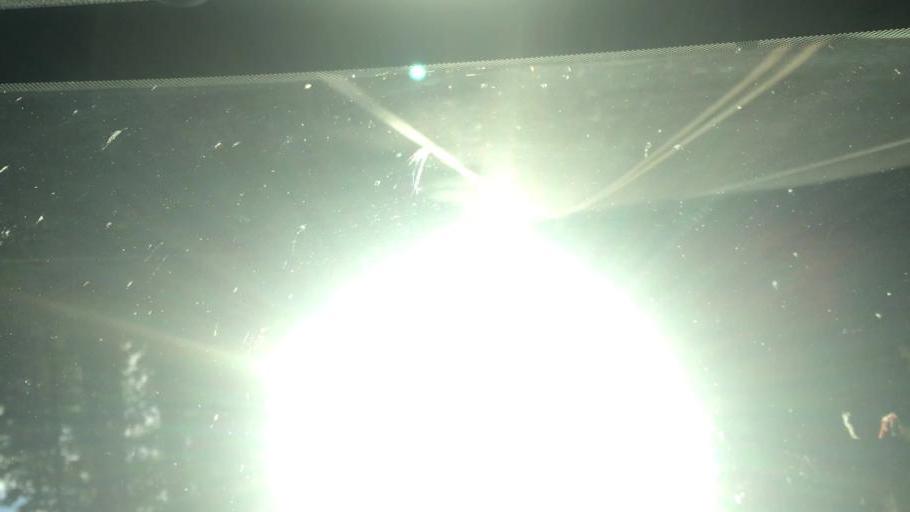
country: US
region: Oregon
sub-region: Deschutes County
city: Deschutes River Woods
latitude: 44.0362
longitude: -121.4574
